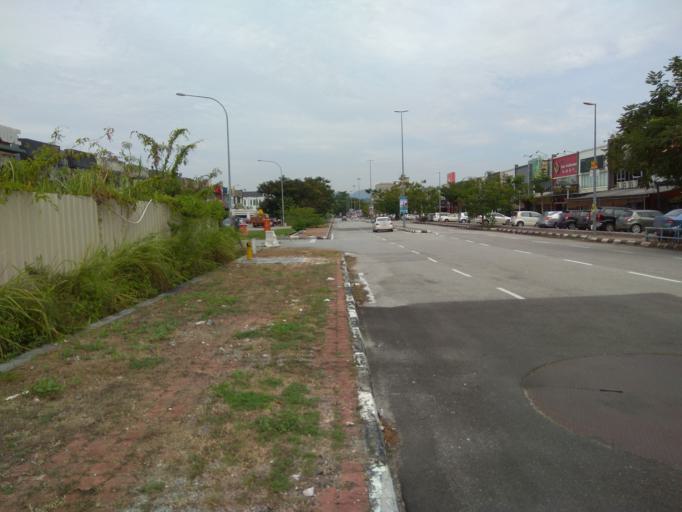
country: MY
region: Perak
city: Ipoh
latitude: 4.6192
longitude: 101.1197
